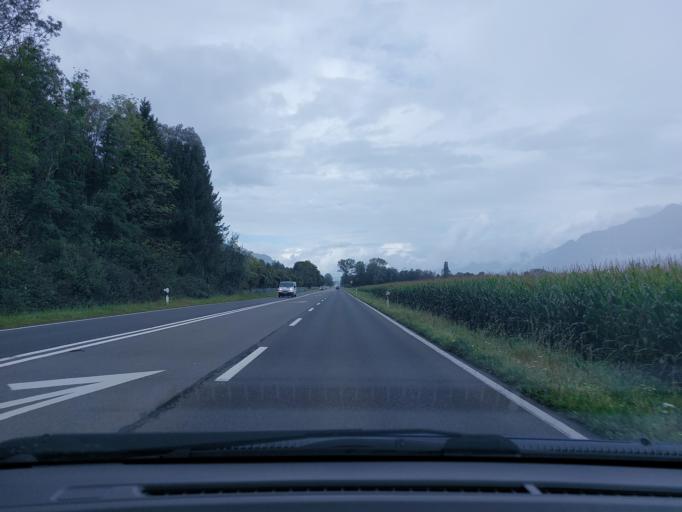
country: CH
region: Valais
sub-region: Monthey District
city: Vionnaz
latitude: 46.2936
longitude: 6.9116
